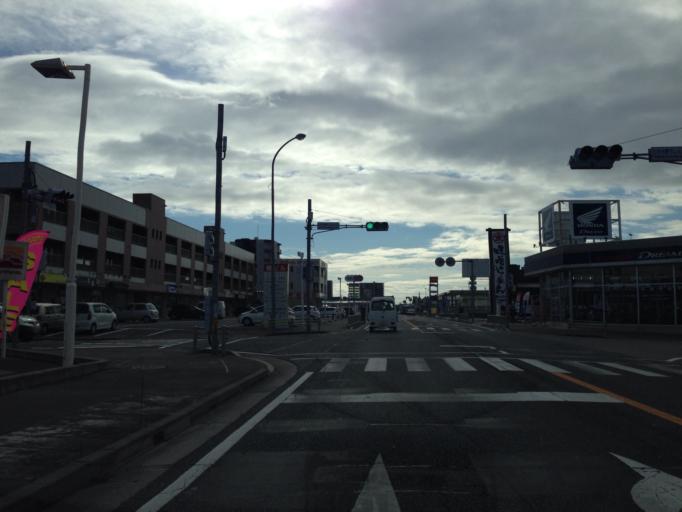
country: JP
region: Ibaraki
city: Naka
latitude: 36.0126
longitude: 140.1565
